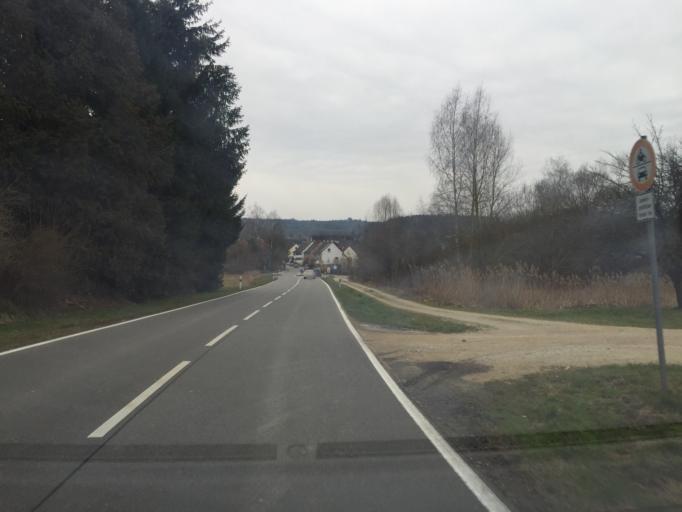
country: DE
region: Baden-Wuerttemberg
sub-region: Freiburg Region
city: Gottmadingen
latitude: 47.7261
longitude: 8.7556
